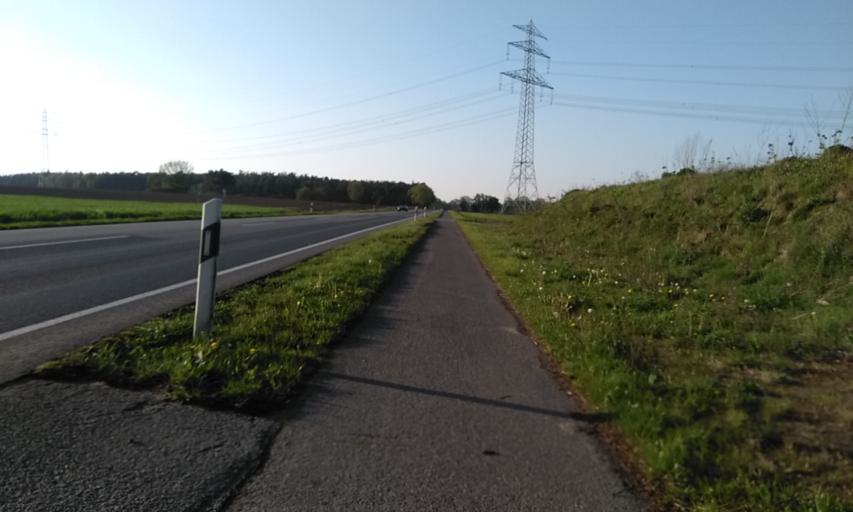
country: DE
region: Lower Saxony
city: Dollern
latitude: 53.5229
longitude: 9.5588
